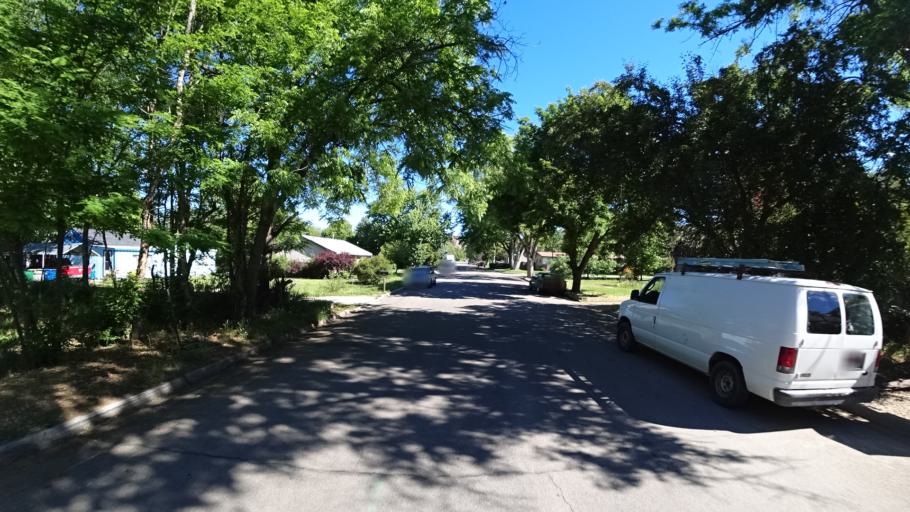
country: US
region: Idaho
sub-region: Ada County
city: Garden City
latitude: 43.6414
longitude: -116.2283
